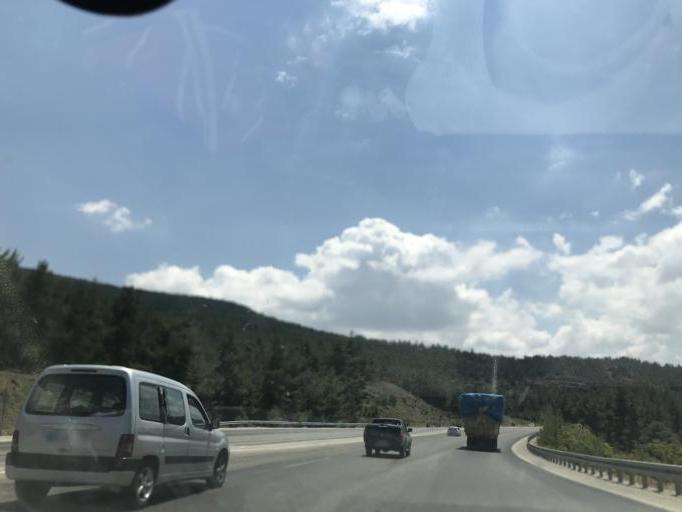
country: TR
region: Denizli
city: Serinhisar
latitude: 37.6536
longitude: 29.2275
